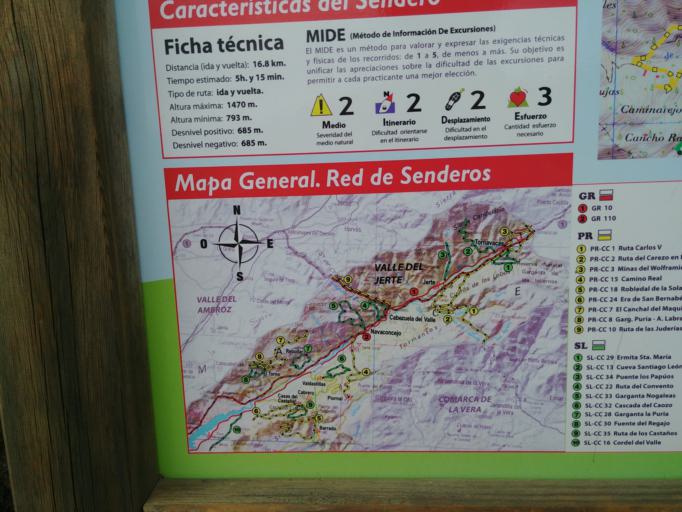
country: ES
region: Extremadura
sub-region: Provincia de Caceres
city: Casas del Castanar
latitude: 40.1374
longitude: -5.9452
